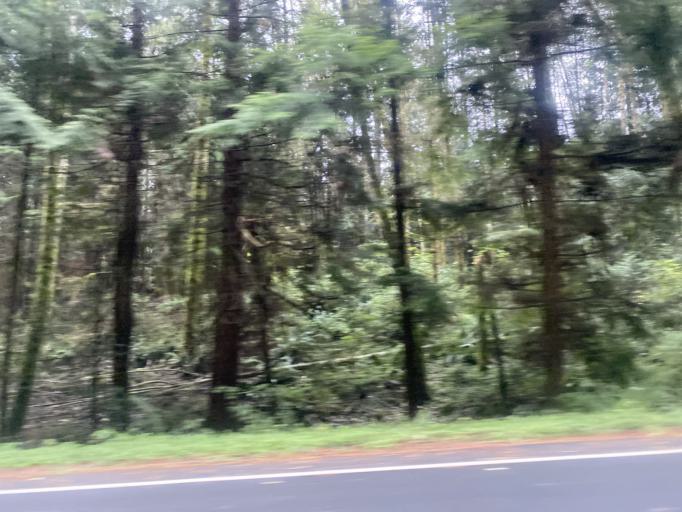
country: US
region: Washington
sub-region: Island County
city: Freeland
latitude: 48.0738
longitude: -122.4850
